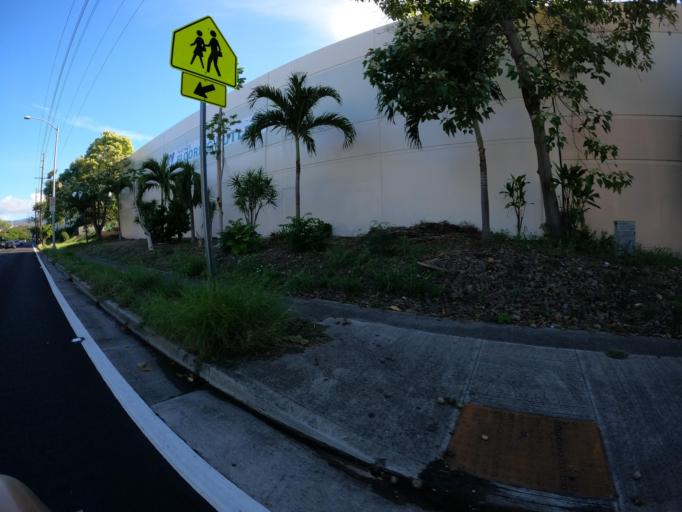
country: US
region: Hawaii
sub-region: Honolulu County
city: Halawa
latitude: 21.3562
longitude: -157.9301
